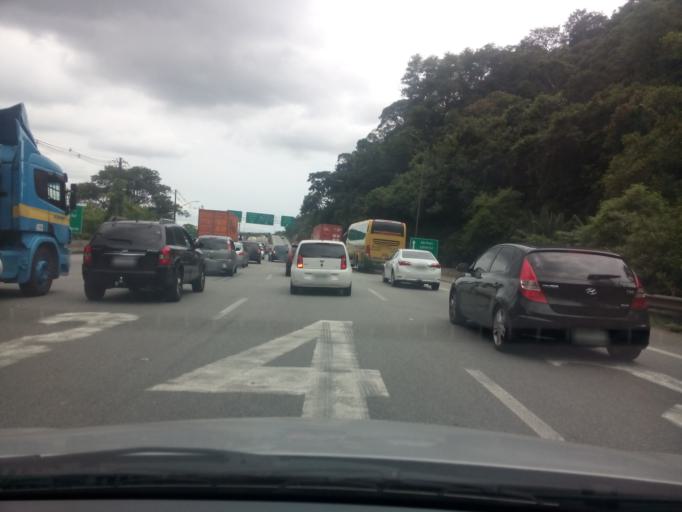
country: BR
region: Sao Paulo
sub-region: Cubatao
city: Cubatao
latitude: -23.8922
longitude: -46.4404
